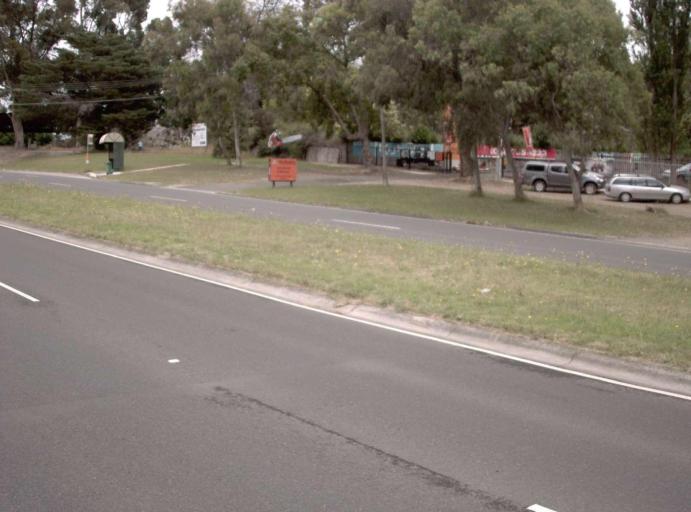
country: AU
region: Victoria
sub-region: Yarra Ranges
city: Lilydale
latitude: -37.7559
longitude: 145.3612
